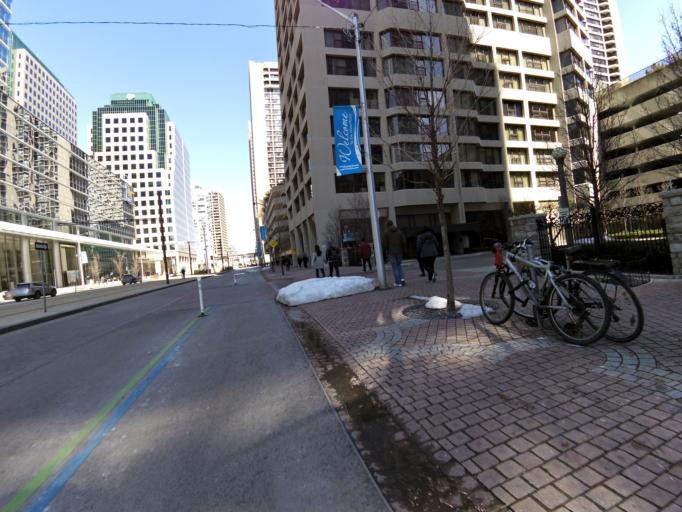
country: CA
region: Ontario
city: Toronto
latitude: 43.6400
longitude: -79.3794
